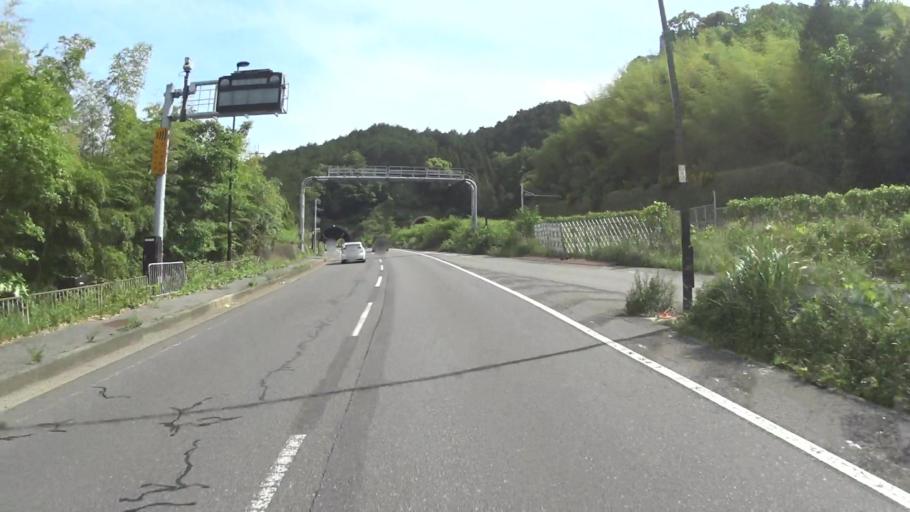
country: JP
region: Shiga Prefecture
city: Otsu-shi
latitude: 35.0231
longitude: 135.8486
